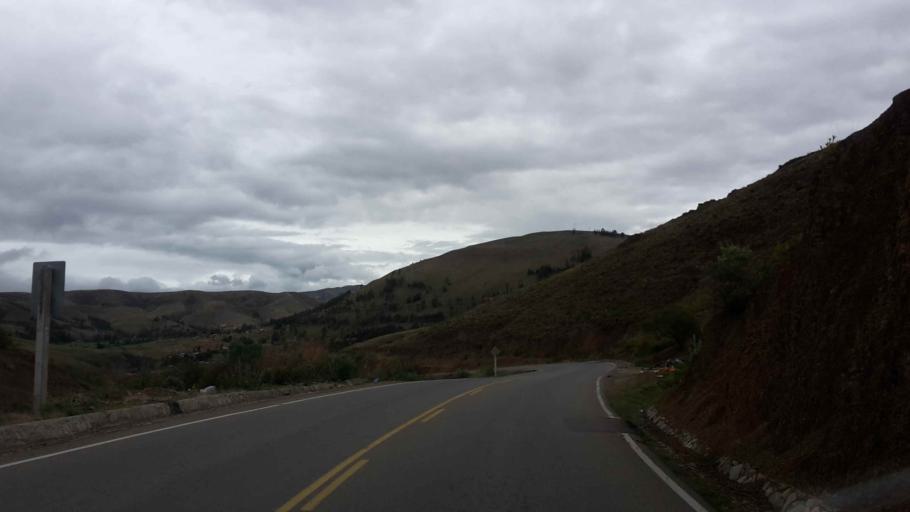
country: BO
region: Cochabamba
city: Punata
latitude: -17.4818
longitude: -65.7761
